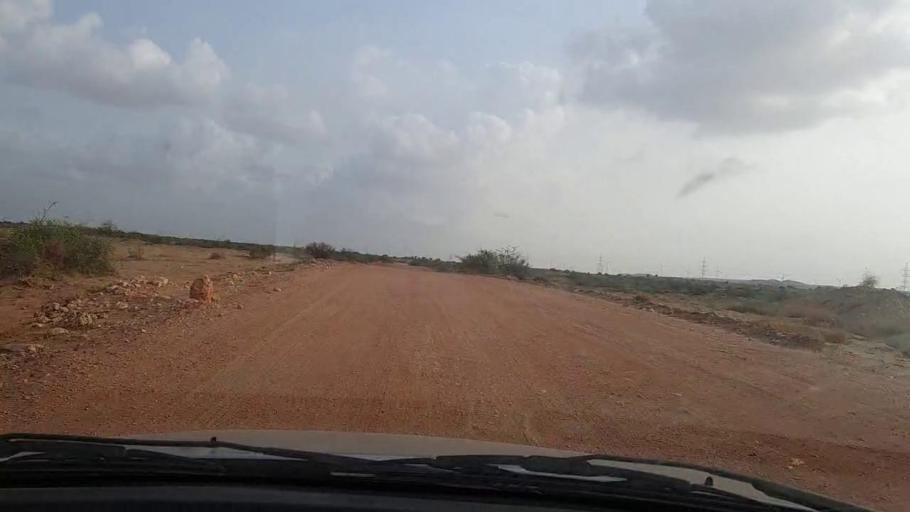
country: PK
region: Sindh
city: Thatta
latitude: 25.0768
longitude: 67.8933
